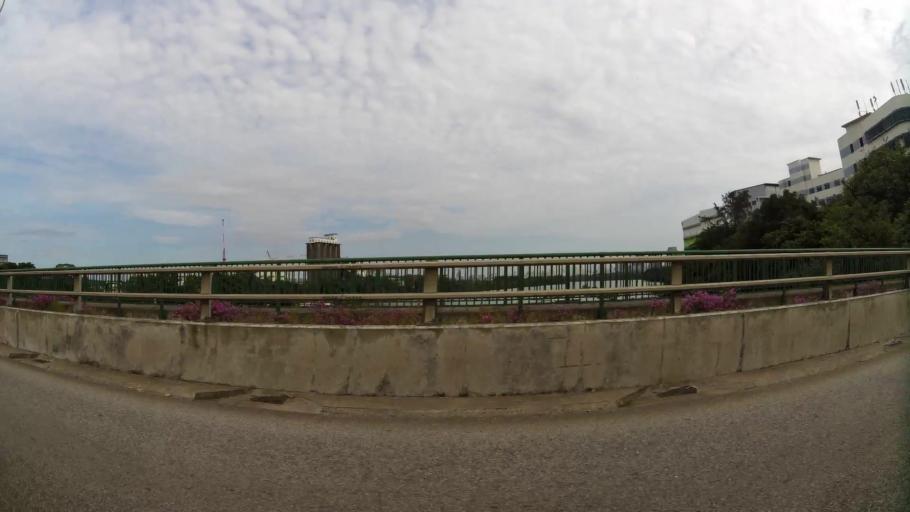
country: SG
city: Singapore
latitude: 1.3127
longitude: 103.7279
